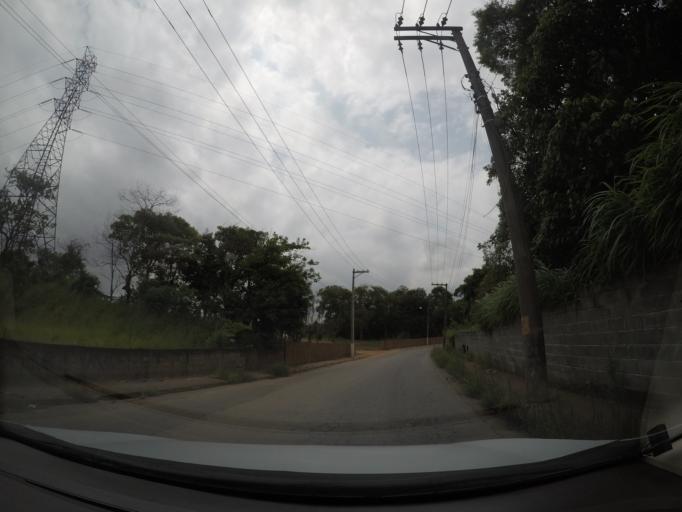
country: BR
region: Sao Paulo
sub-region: Itaquaquecetuba
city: Itaquaquecetuba
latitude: -23.4506
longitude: -46.3871
